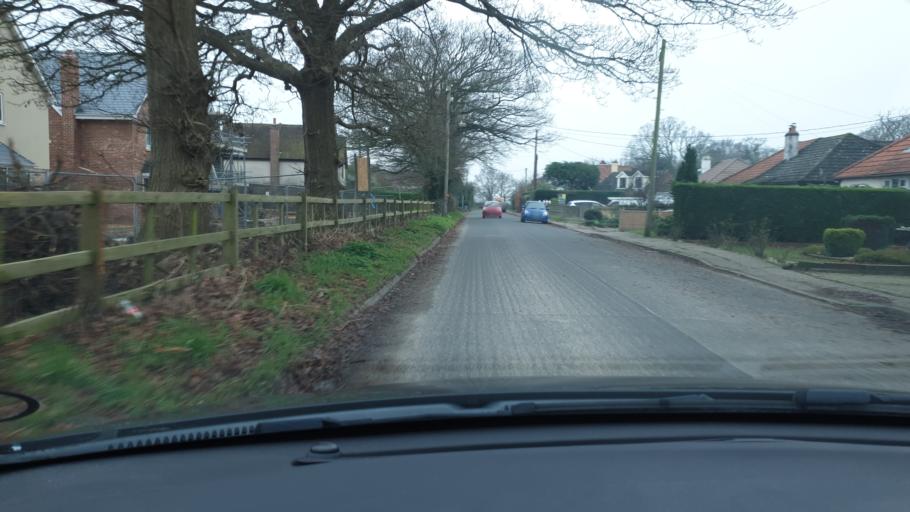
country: GB
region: England
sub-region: Essex
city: Great Bentley
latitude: 51.8400
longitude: 1.0722
